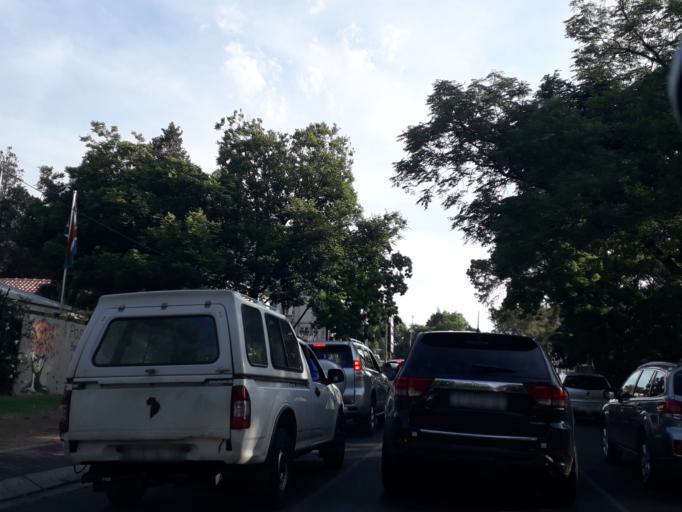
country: ZA
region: Gauteng
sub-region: City of Johannesburg Metropolitan Municipality
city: Johannesburg
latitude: -26.1140
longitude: 28.0224
